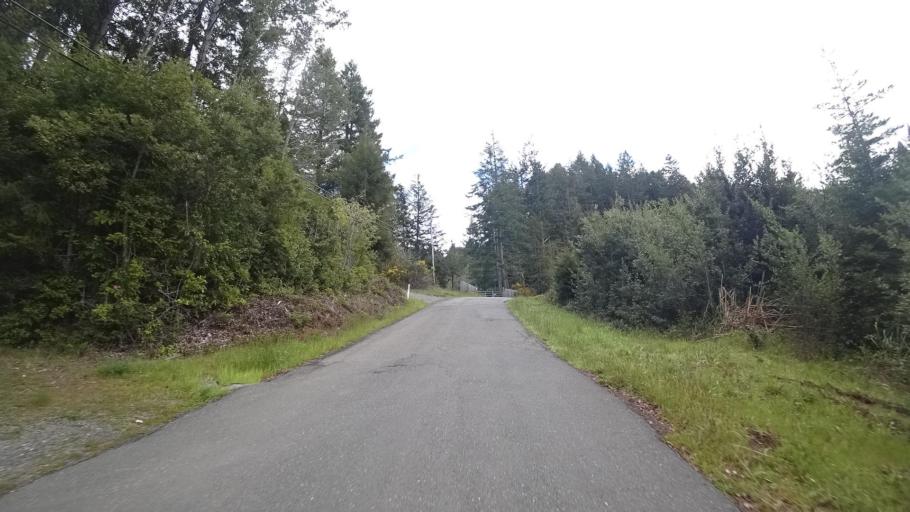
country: US
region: California
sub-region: Humboldt County
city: Blue Lake
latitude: 40.8248
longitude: -124.0021
